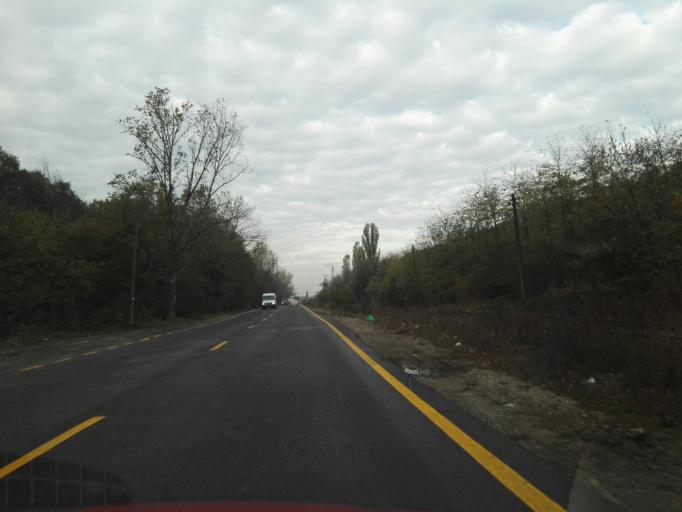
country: RO
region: Ilfov
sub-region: Comuna Magurele
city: Magurele
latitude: 44.3556
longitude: 26.0478
